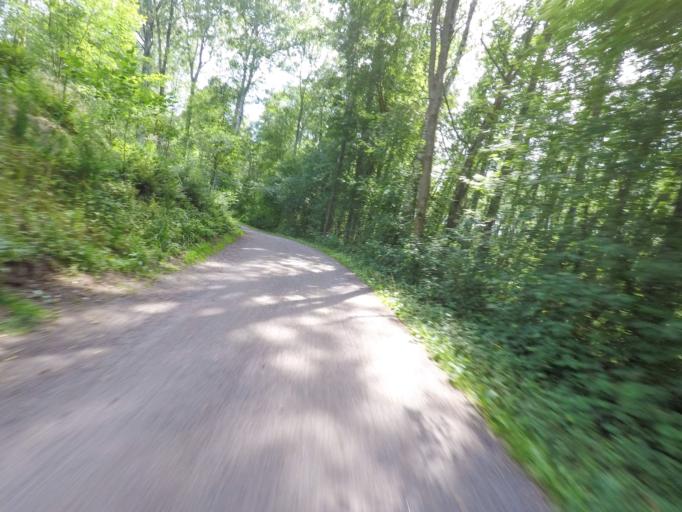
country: FI
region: Uusimaa
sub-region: Helsinki
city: Vantaa
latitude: 60.2072
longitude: 25.0278
